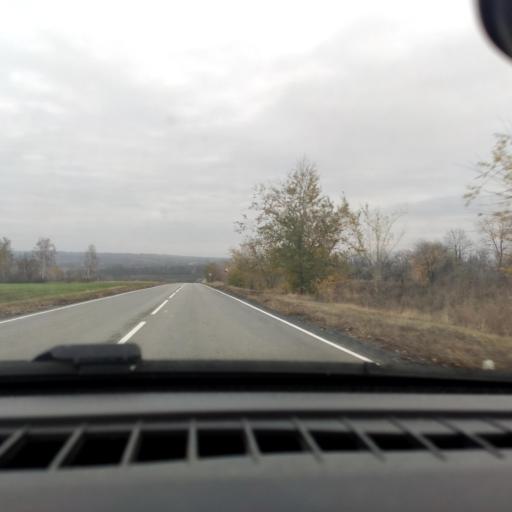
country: RU
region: Voronezj
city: Ostrogozhsk
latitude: 50.7656
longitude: 38.8738
